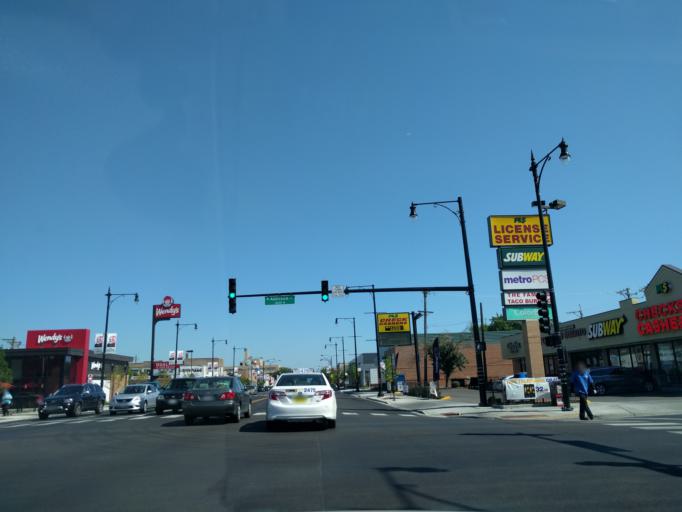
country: US
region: Illinois
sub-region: Cook County
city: Lincolnwood
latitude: 41.9466
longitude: -87.6882
